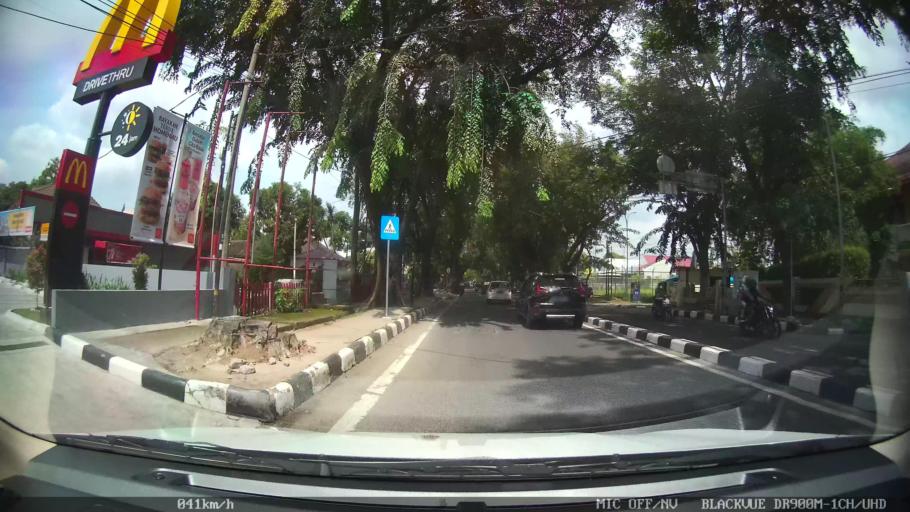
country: ID
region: North Sumatra
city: Medan
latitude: 3.5712
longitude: 98.6697
